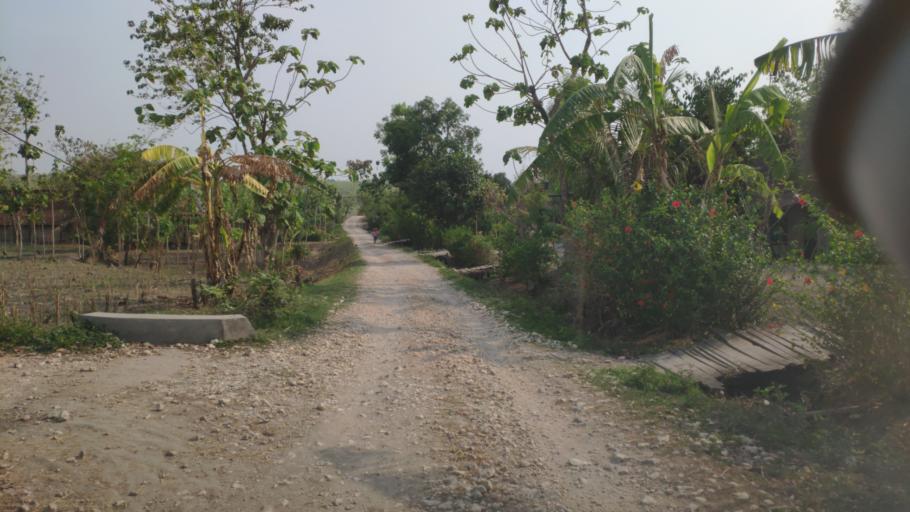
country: ID
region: Central Java
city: Randublatung
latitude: -7.2825
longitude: 111.2457
